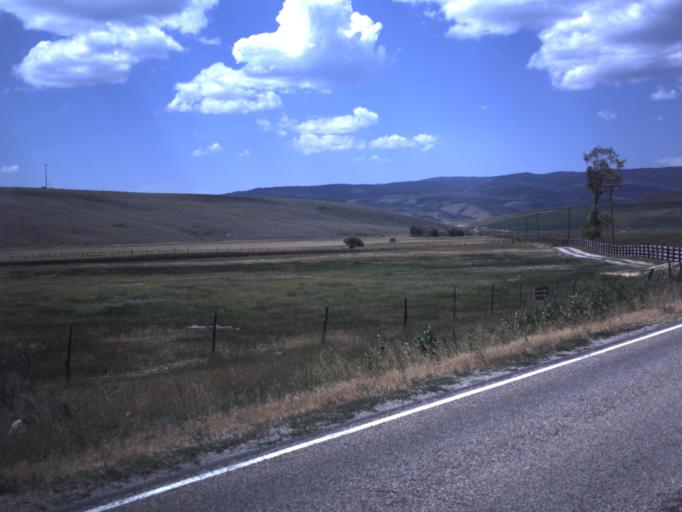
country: US
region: Utah
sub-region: Rich County
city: Randolph
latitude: 41.8389
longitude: -111.3400
